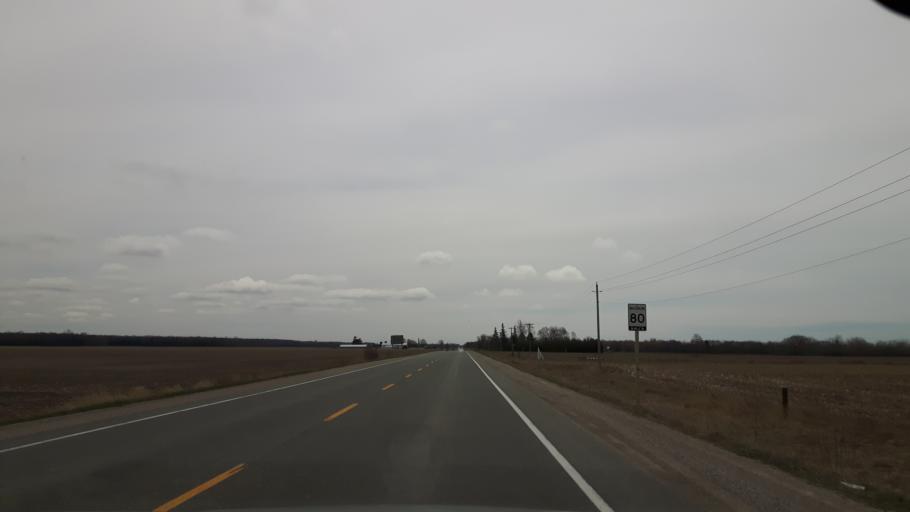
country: CA
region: Ontario
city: Goderich
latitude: 43.6405
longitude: -81.7057
